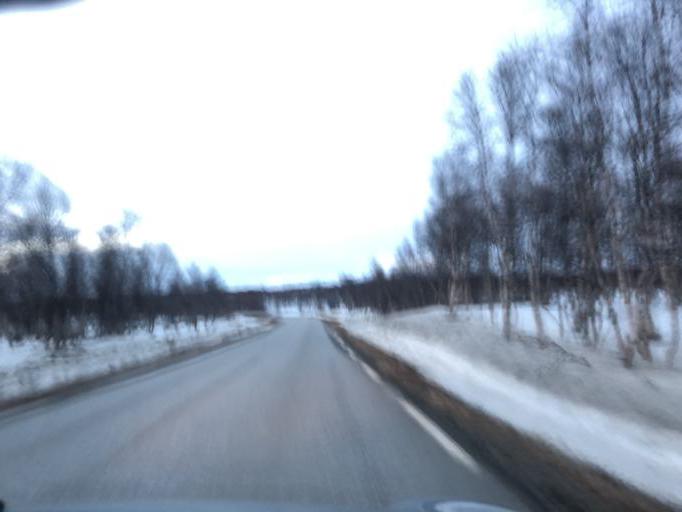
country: NO
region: Sor-Trondelag
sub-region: Tydal
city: Aas
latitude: 62.7217
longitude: 11.8253
